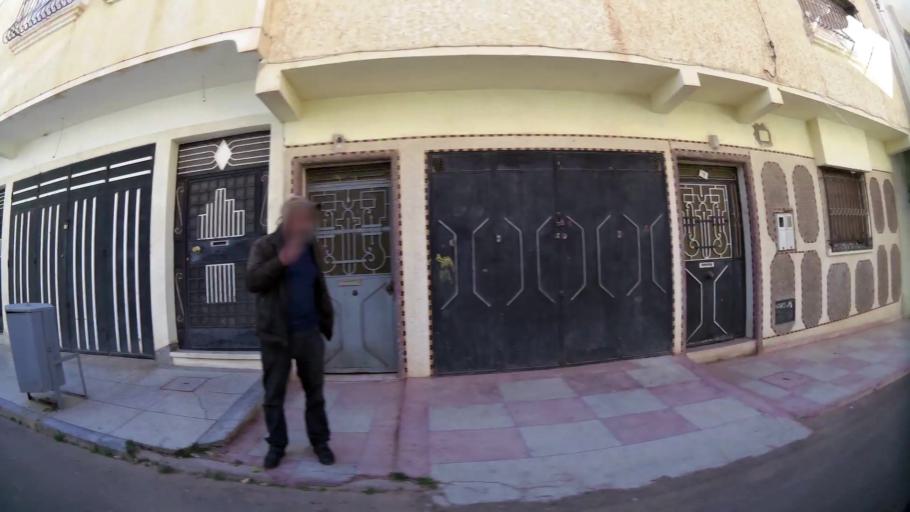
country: MA
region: Oriental
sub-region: Oujda-Angad
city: Oujda
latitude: 34.6569
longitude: -1.9179
